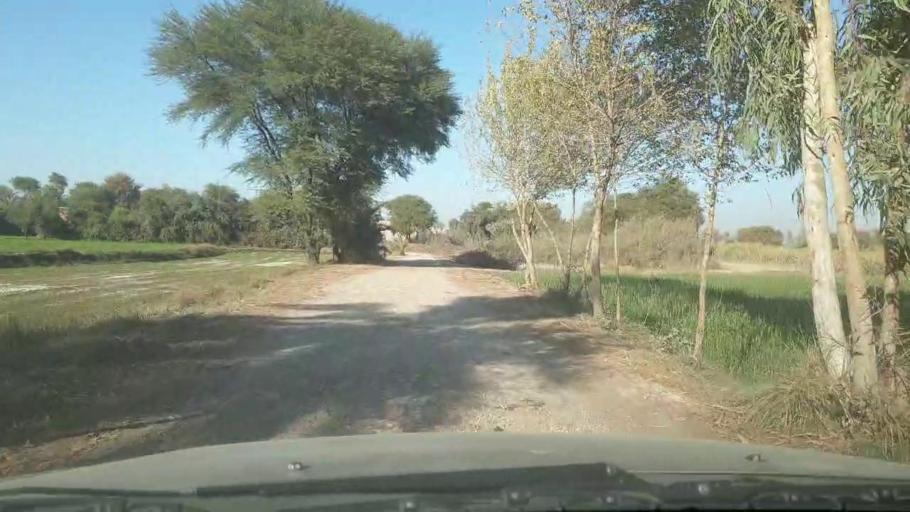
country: PK
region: Sindh
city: Adilpur
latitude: 27.9607
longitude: 69.2024
